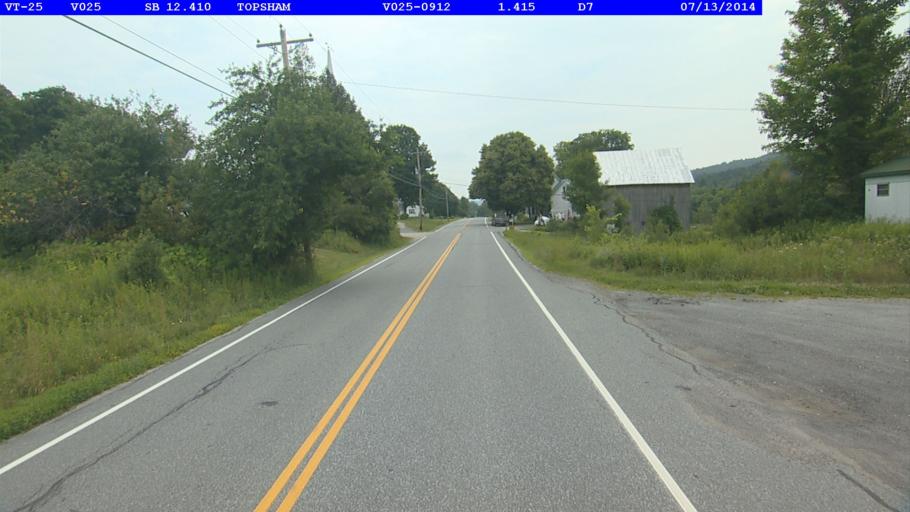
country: US
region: Vermont
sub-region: Orange County
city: Chelsea
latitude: 44.0900
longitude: -72.2834
